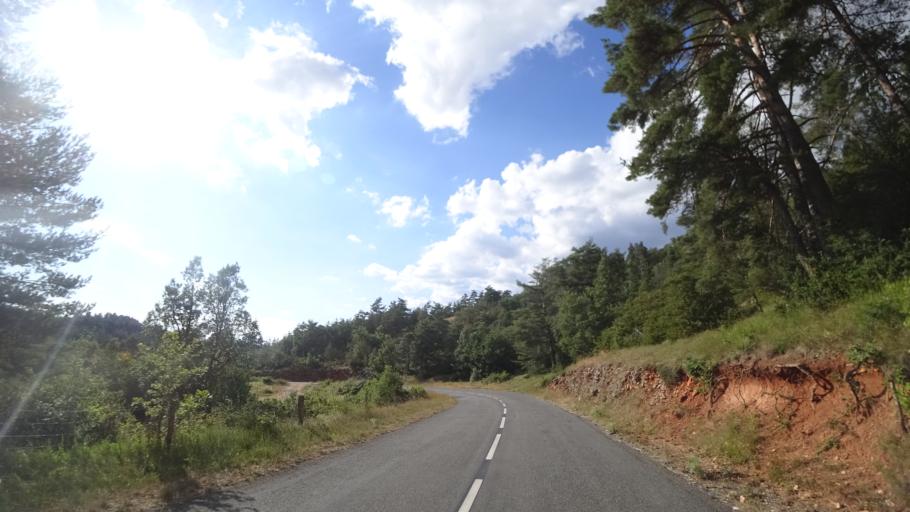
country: FR
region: Languedoc-Roussillon
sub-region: Departement de la Lozere
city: Chanac
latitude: 44.3794
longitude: 3.3226
